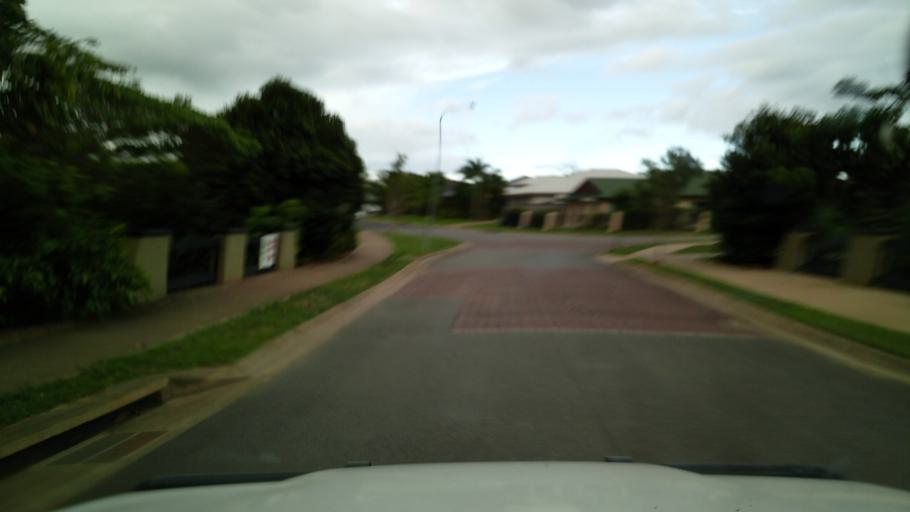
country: AU
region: Queensland
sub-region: Cairns
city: Redlynch
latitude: -16.8428
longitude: 145.6885
